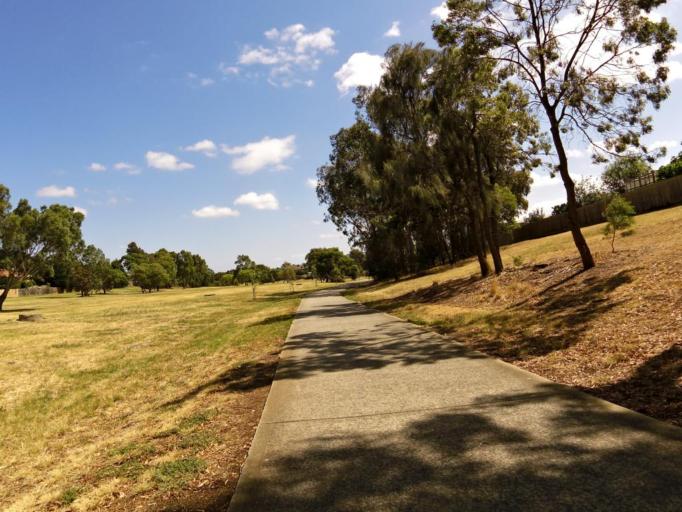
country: AU
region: Victoria
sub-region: Hume
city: Meadow Heights
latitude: -37.6446
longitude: 144.9195
